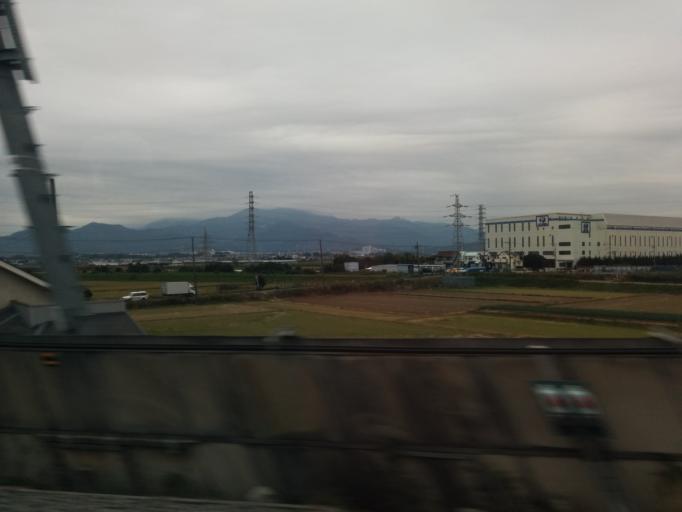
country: JP
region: Kanagawa
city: Isehara
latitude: 35.3798
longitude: 139.3539
